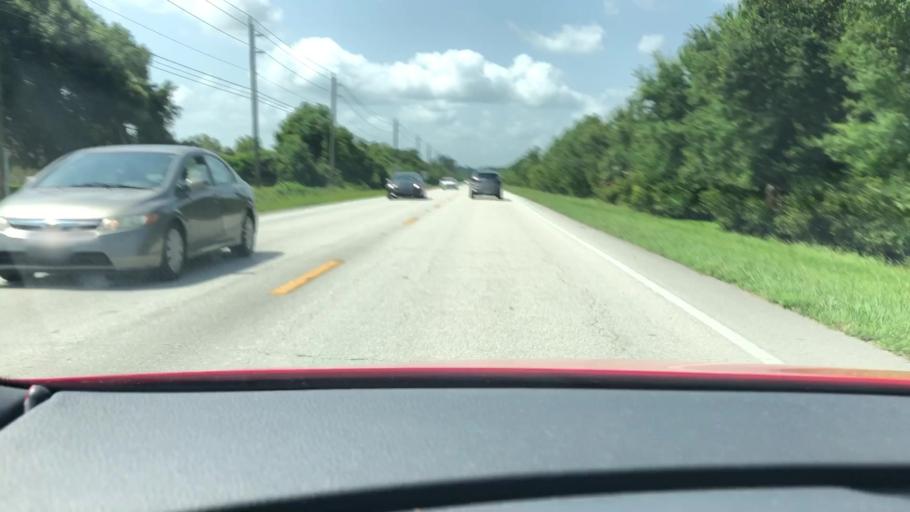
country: US
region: Florida
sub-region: Volusia County
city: Samsula-Spruce Creek
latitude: 29.0690
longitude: -81.0681
